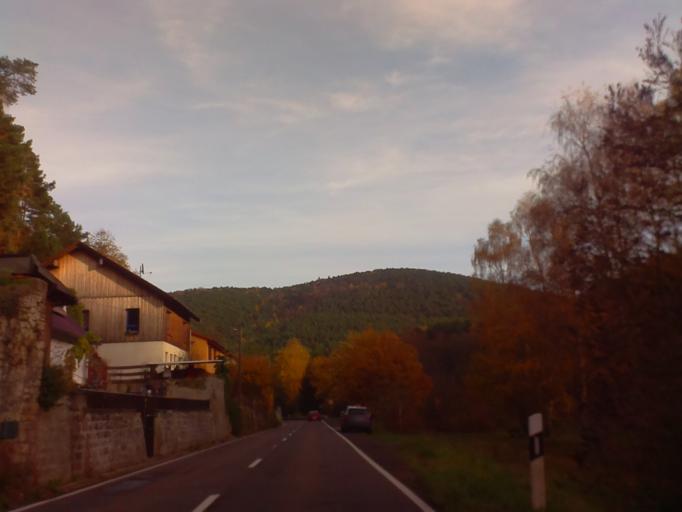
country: DE
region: Rheinland-Pfalz
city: Altleiningen
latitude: 49.5126
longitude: 8.0894
